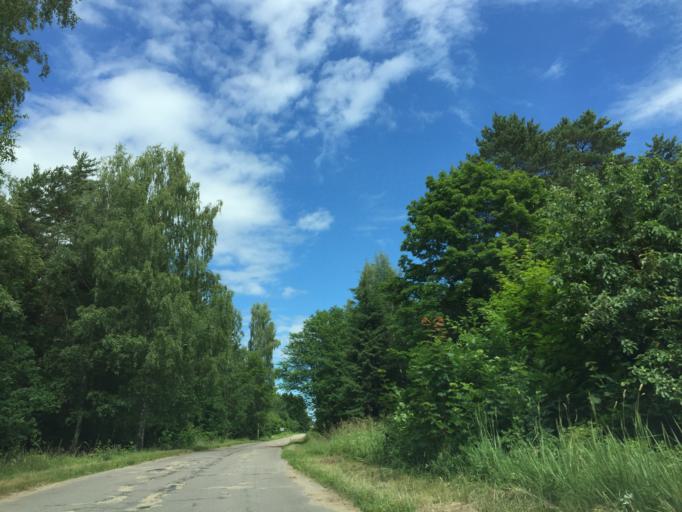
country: LV
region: Saulkrastu
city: Saulkrasti
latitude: 57.4090
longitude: 24.4233
